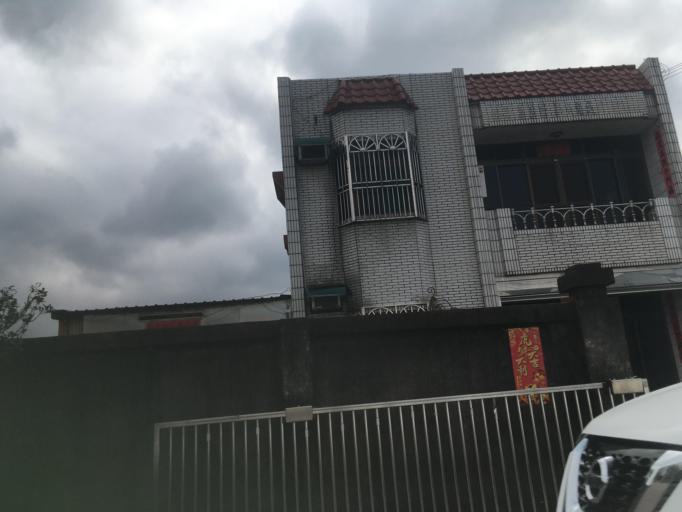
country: TW
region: Taiwan
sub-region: Miaoli
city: Miaoli
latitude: 24.4414
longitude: 120.7094
